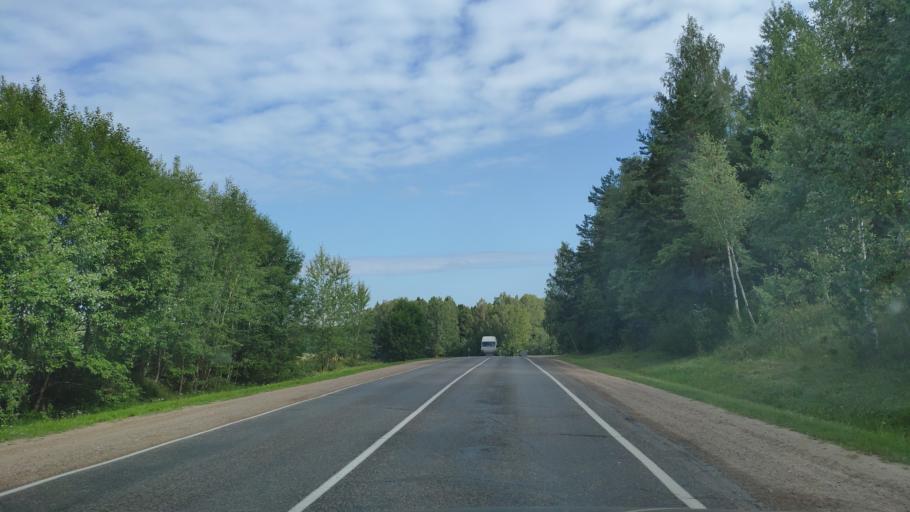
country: BY
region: Minsk
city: Zaslawye
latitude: 53.9634
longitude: 27.2447
